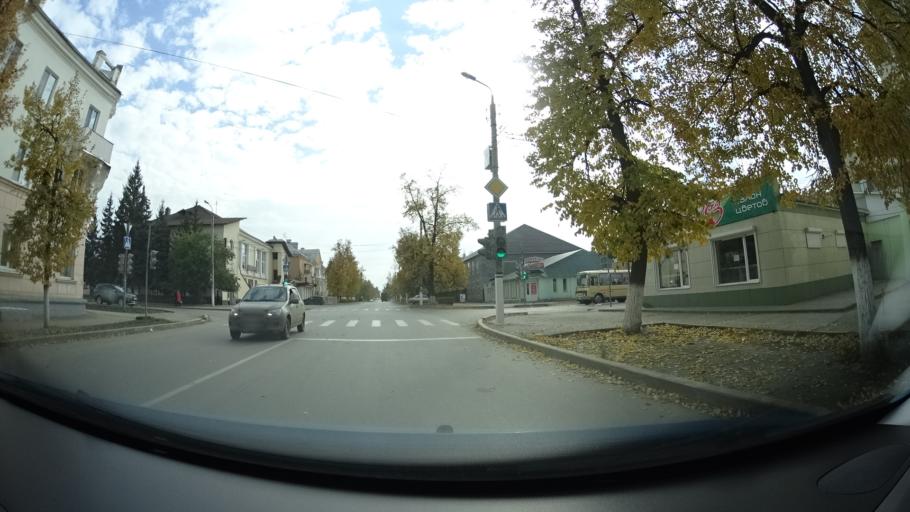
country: RU
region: Bashkortostan
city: Oktyabr'skiy
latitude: 54.4897
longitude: 53.4578
